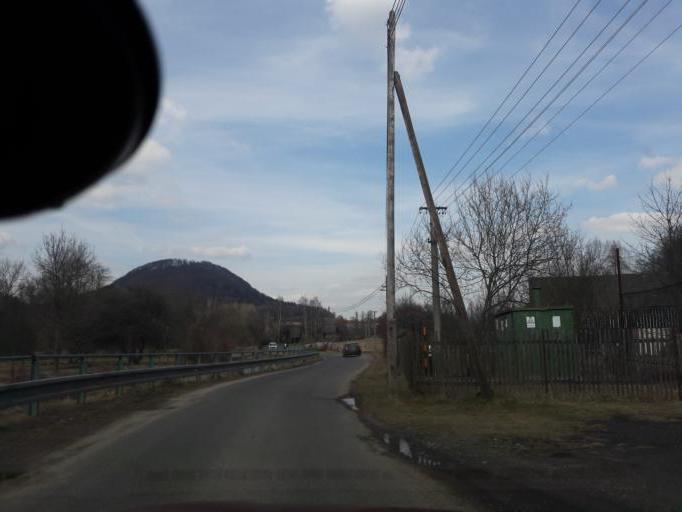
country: CZ
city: Cvikov
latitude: 50.7326
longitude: 14.6365
